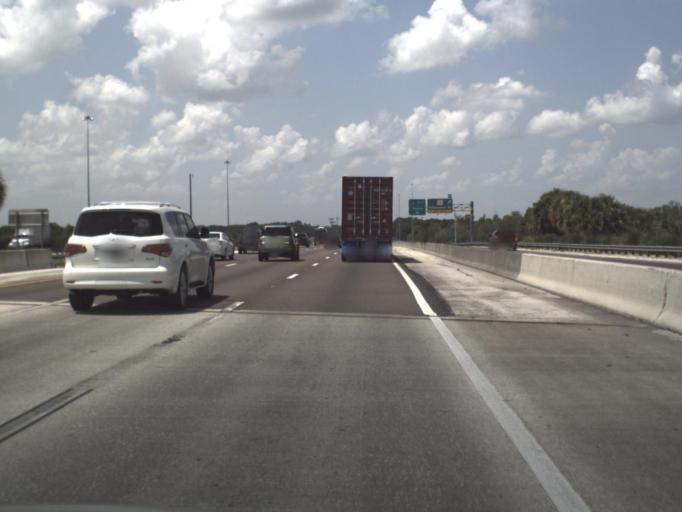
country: US
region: Florida
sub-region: Hillsborough County
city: Plant City
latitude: 28.0324
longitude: -82.1342
